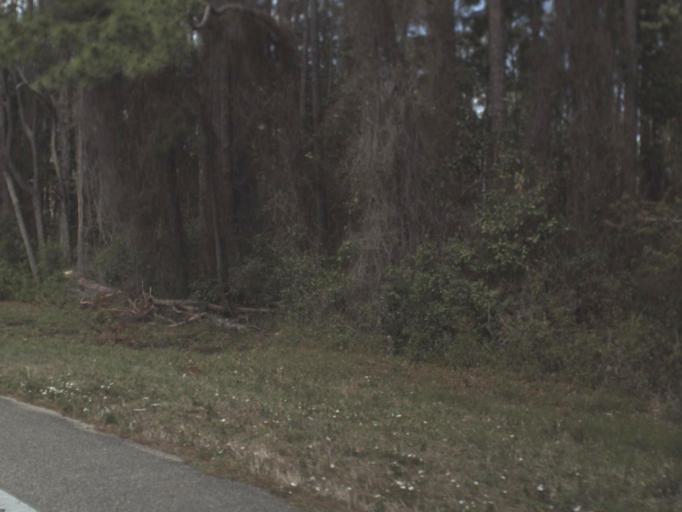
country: US
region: Florida
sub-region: Gulf County
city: Port Saint Joe
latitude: 29.7360
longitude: -85.1615
